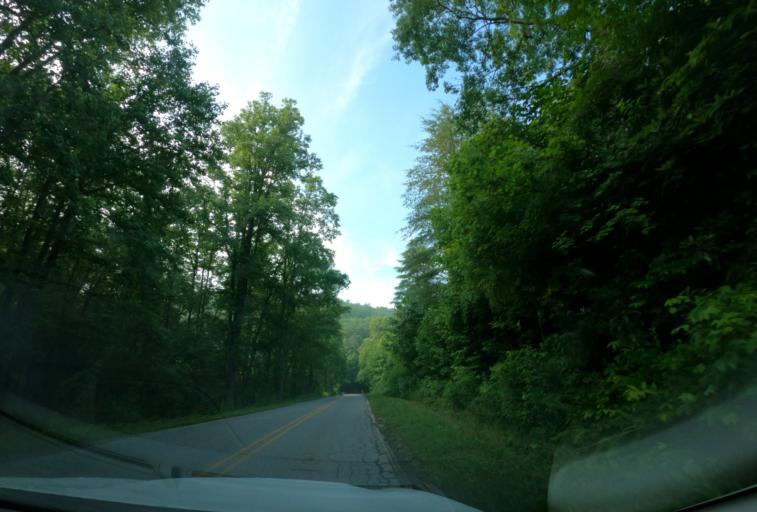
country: US
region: North Carolina
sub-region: Transylvania County
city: Brevard
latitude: 35.2276
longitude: -82.8588
